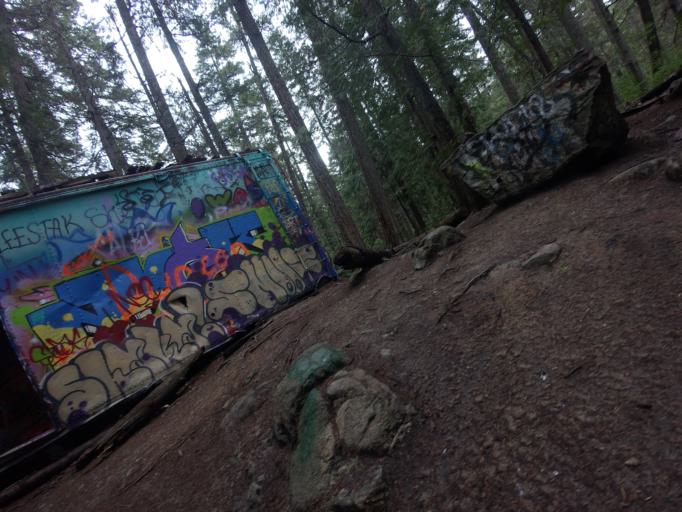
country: CA
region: British Columbia
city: Whistler
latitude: 50.0805
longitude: -123.0562
